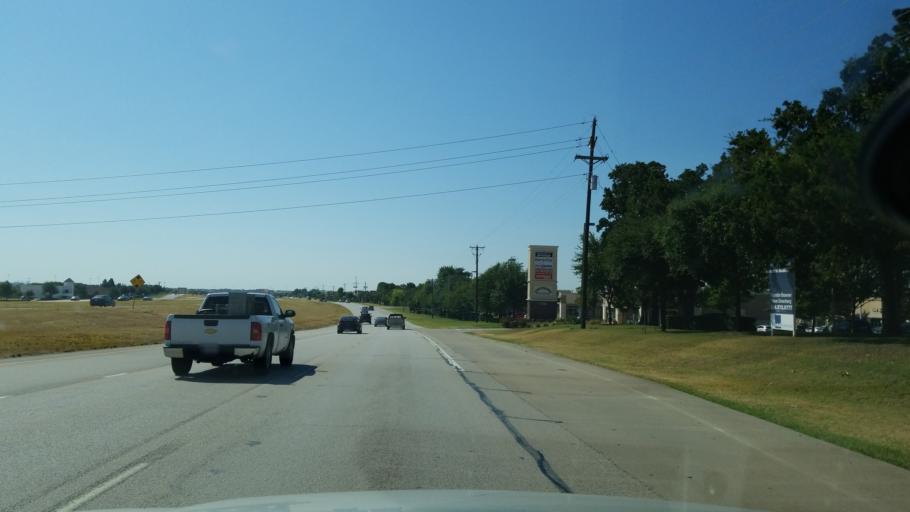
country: US
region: Texas
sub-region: Tarrant County
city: Mansfield
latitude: 32.5875
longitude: -97.1398
